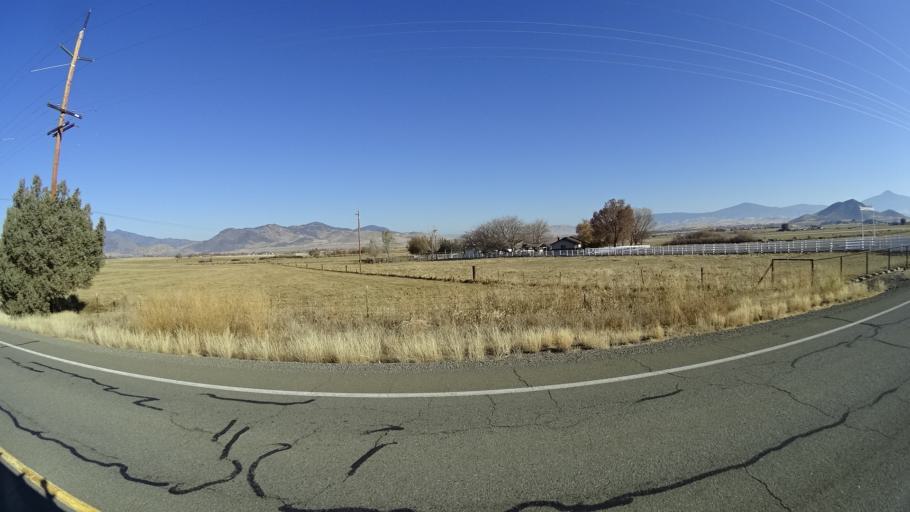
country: US
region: California
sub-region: Siskiyou County
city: Montague
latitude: 41.7081
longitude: -122.5710
